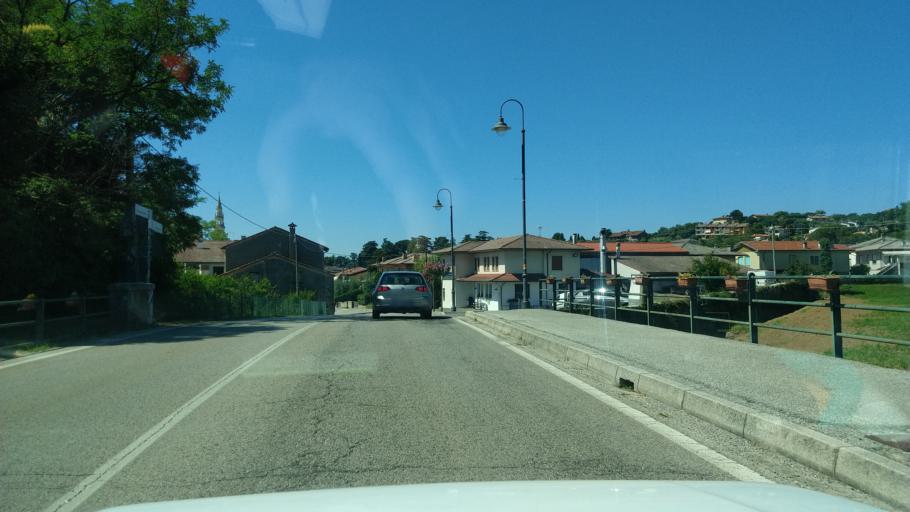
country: IT
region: Veneto
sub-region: Provincia di Vicenza
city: Mason Vicentino
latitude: 45.7217
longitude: 11.6102
